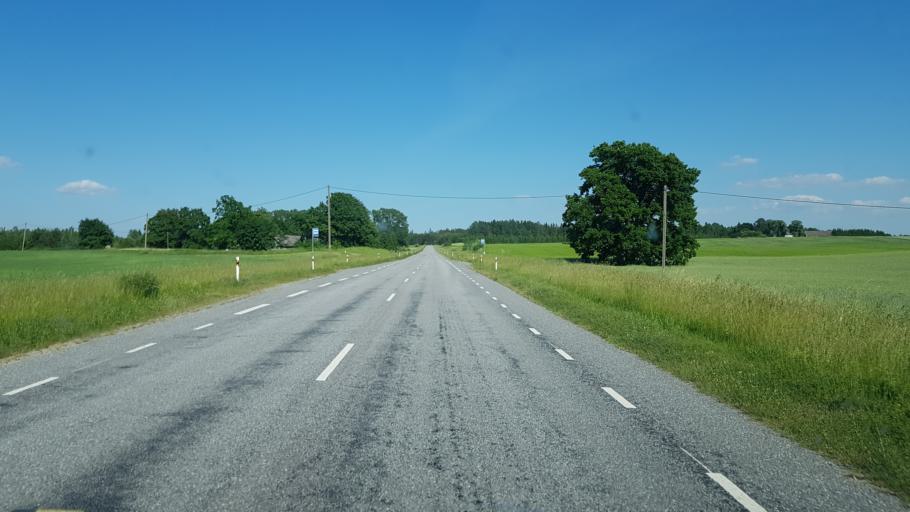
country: EE
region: Vorumaa
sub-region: Voru linn
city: Voru
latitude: 57.8577
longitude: 27.2174
